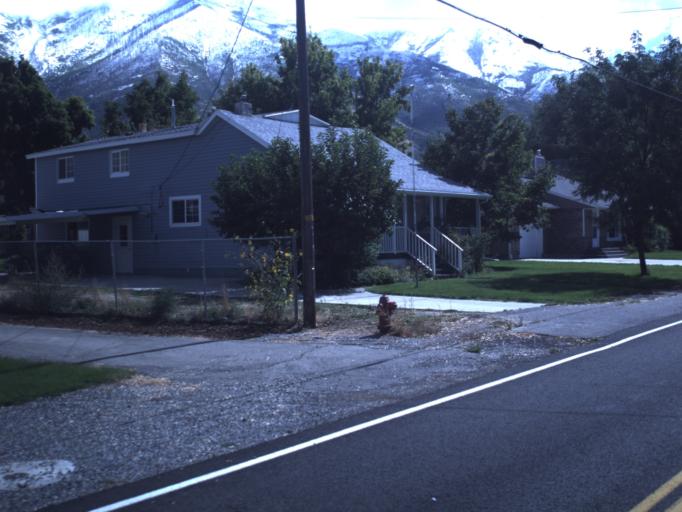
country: US
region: Utah
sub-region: Utah County
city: Mapleton
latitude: 40.1196
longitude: -111.5787
